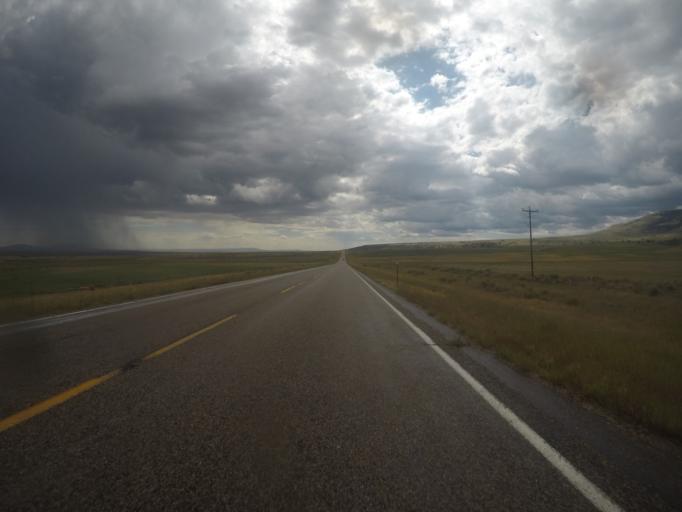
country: US
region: Utah
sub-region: Daggett County
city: Manila
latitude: 41.0234
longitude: -109.9102
